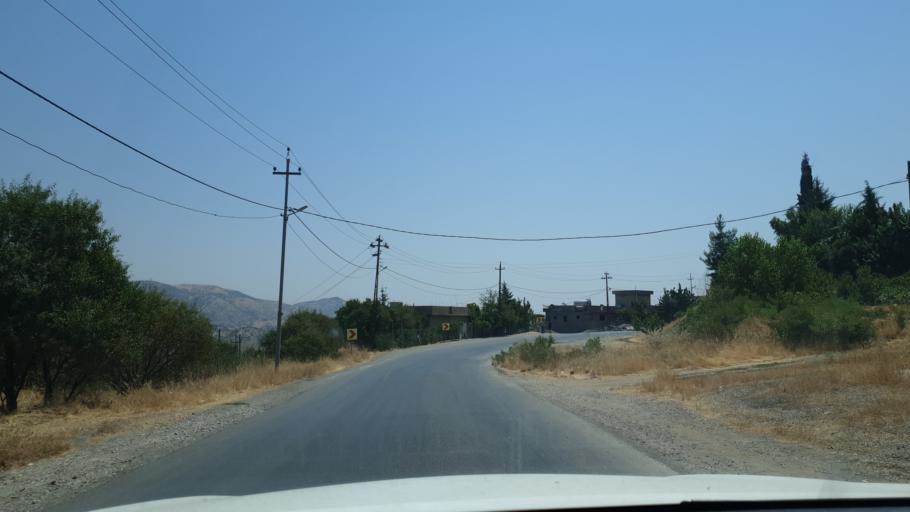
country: IQ
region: Arbil
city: Nahiyat Hiran
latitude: 36.2889
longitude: 44.4842
